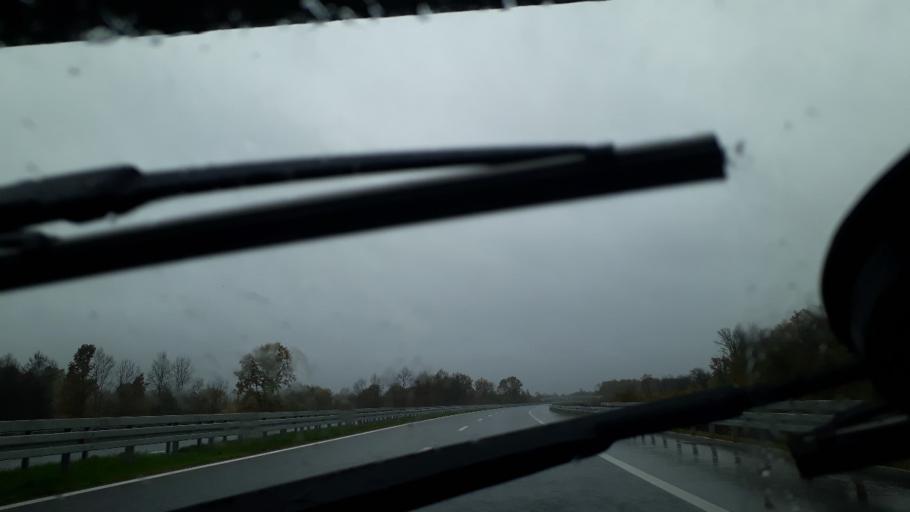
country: BA
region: Republika Srpska
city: Stanari
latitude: 44.8259
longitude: 17.8110
